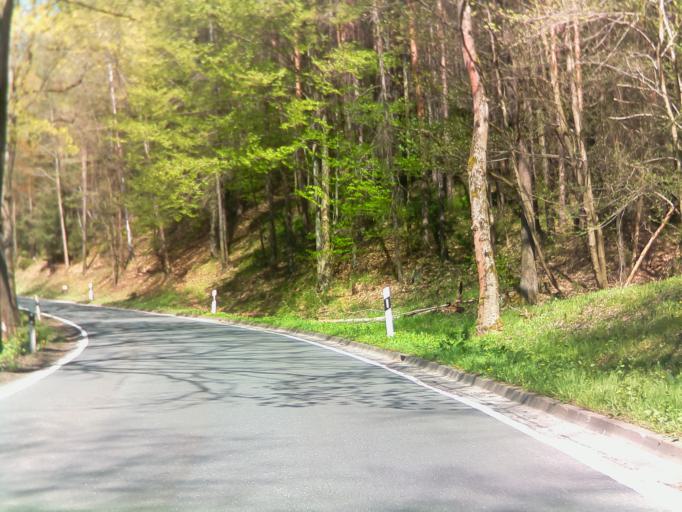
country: DE
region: Thuringia
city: Konigsee
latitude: 50.7086
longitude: 11.0932
